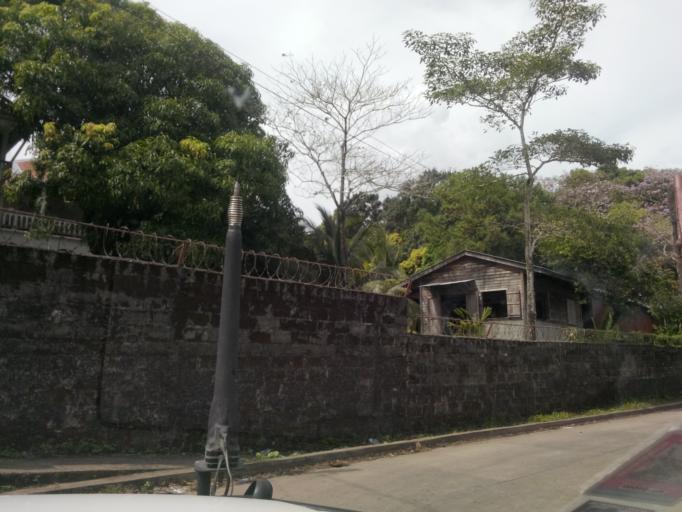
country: NI
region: Atlantico Sur
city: Bluefields
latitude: 12.0085
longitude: -83.7659
